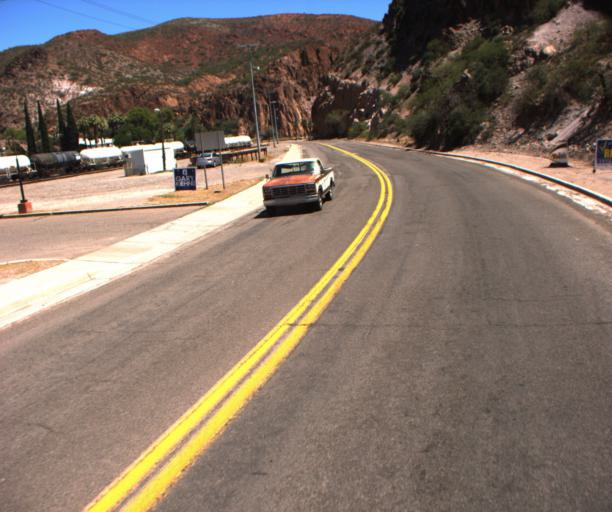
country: US
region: Arizona
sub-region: Greenlee County
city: Clifton
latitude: 33.0542
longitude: -109.2981
